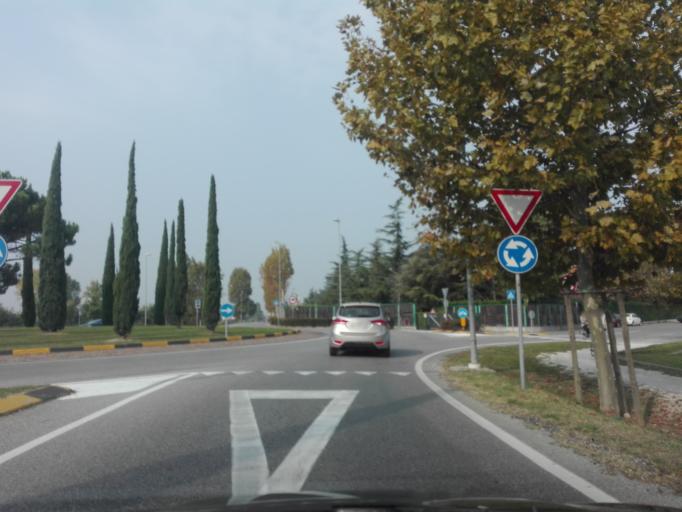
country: IT
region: Lombardy
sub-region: Provincia di Brescia
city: San Martino della Battaglia
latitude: 45.4566
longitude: 10.6404
